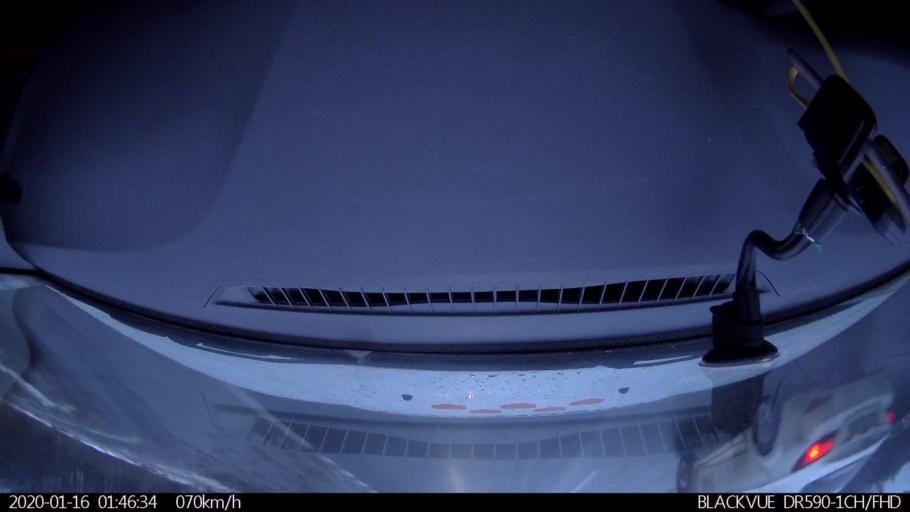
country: RU
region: Nizjnij Novgorod
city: Gorbatovka
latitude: 56.3103
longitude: 43.7835
